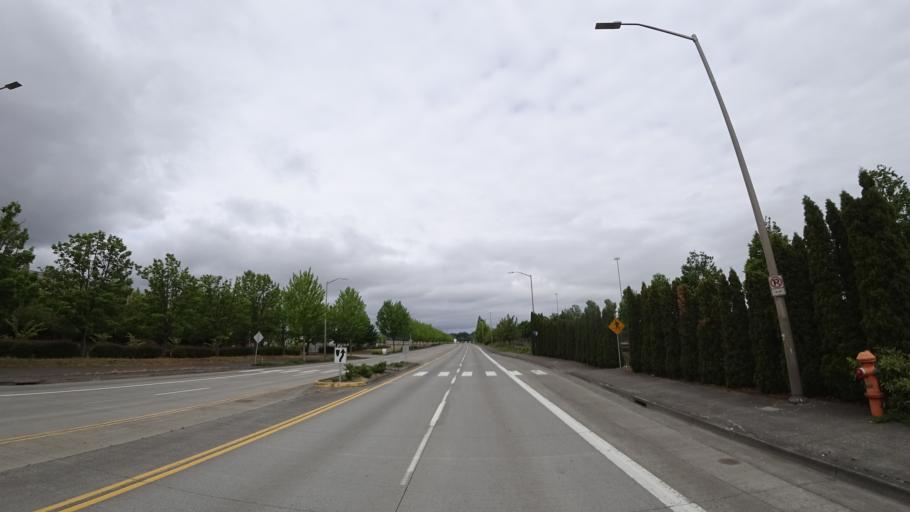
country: US
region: Washington
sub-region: Clark County
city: Lake Shore
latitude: 45.6327
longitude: -122.7496
